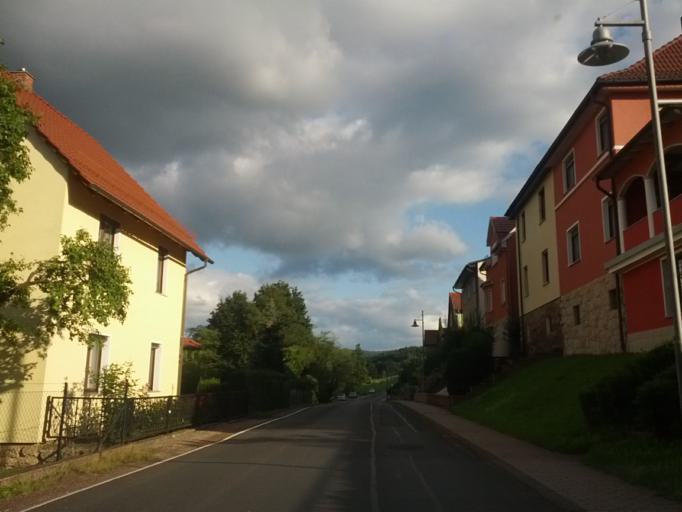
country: DE
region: Thuringia
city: Wolfsburg-Unkeroda
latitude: 50.9349
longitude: 10.2692
